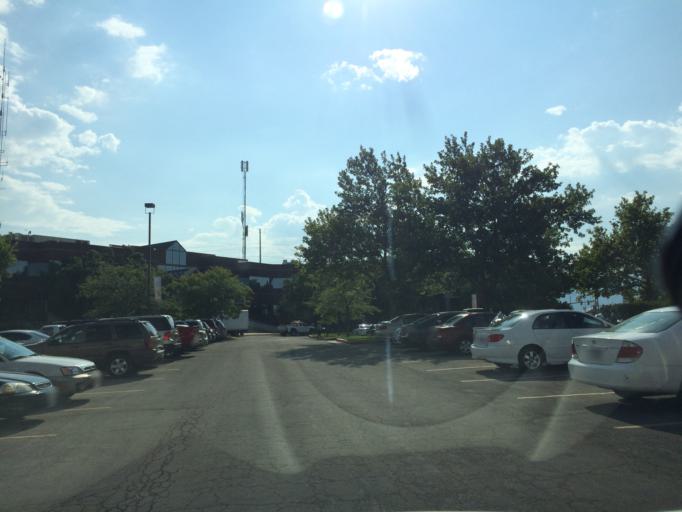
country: US
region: Utah
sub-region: Salt Lake County
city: Taylorsville
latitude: 40.6939
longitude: -111.9598
